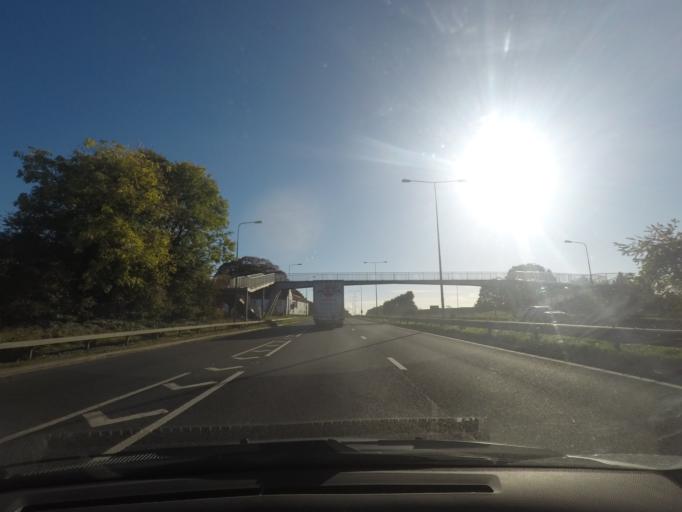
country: GB
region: England
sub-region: East Riding of Yorkshire
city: Welton
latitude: 53.7313
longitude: -0.5521
